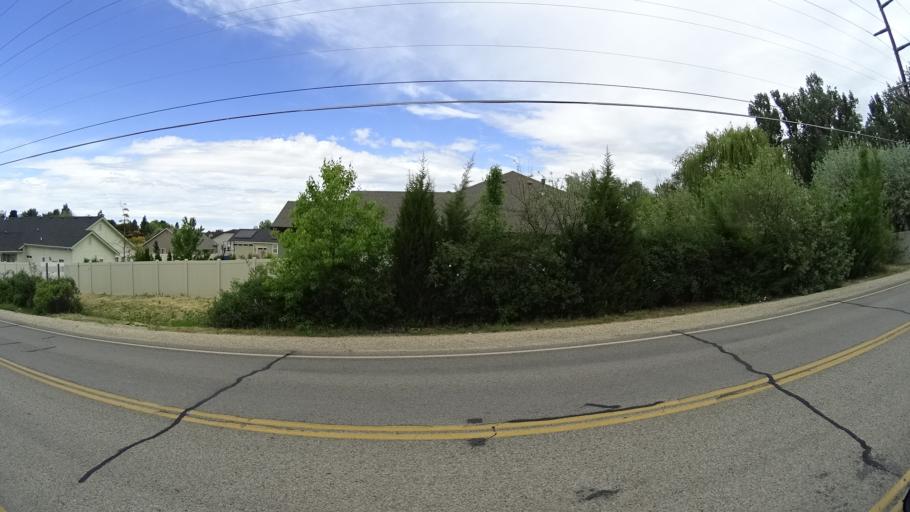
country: US
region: Idaho
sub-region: Ada County
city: Meridian
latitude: 43.5757
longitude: -116.3252
